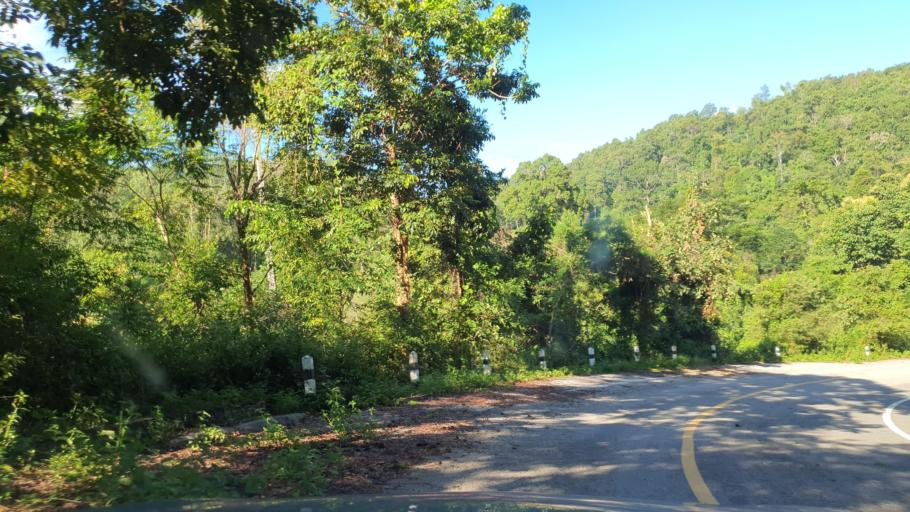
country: TH
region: Chiang Mai
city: Mae On
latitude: 18.7985
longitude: 99.3017
